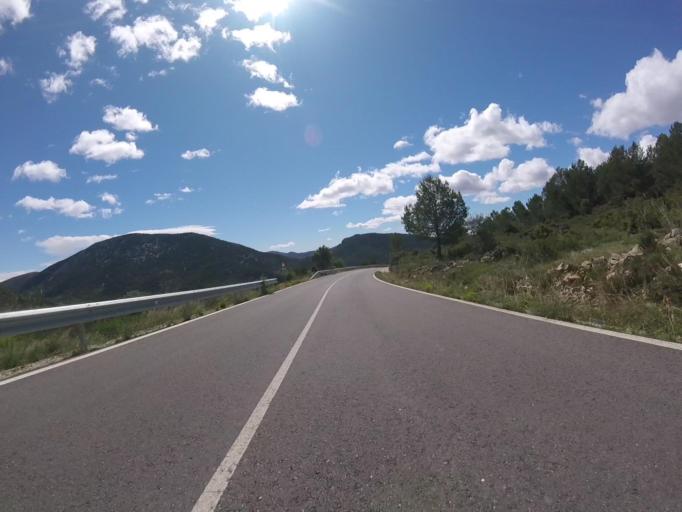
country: ES
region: Valencia
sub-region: Provincia de Castello
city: Culla
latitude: 40.2970
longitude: -0.1184
